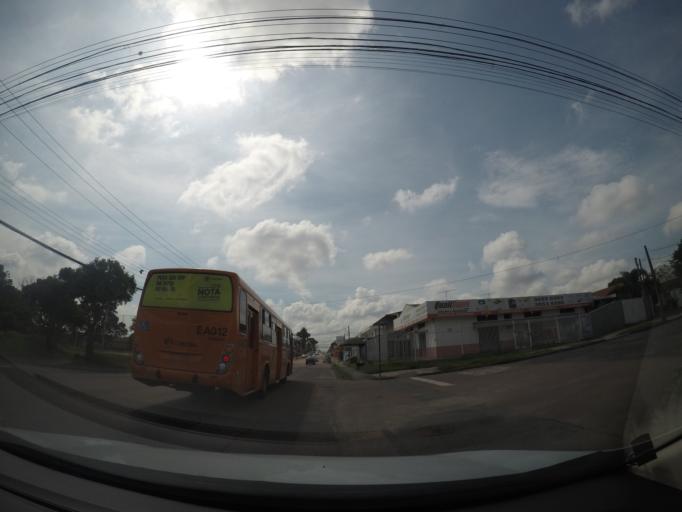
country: BR
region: Parana
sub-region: Curitiba
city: Curitiba
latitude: -25.4899
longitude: -49.2760
